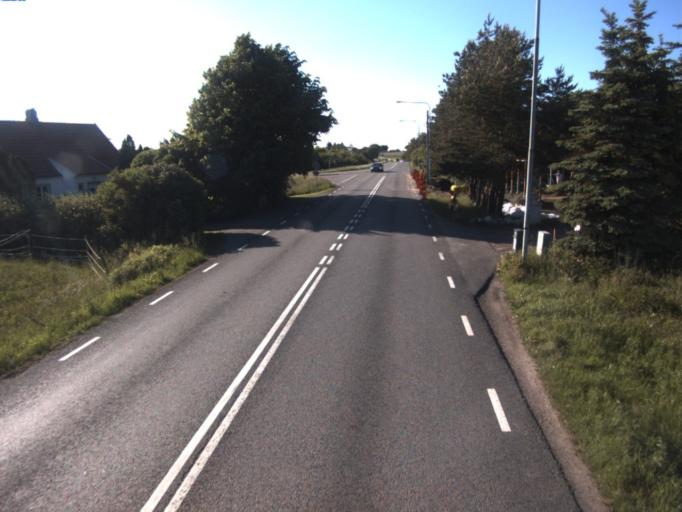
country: SE
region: Skane
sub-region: Helsingborg
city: Rydeback
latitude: 55.9730
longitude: 12.7784
